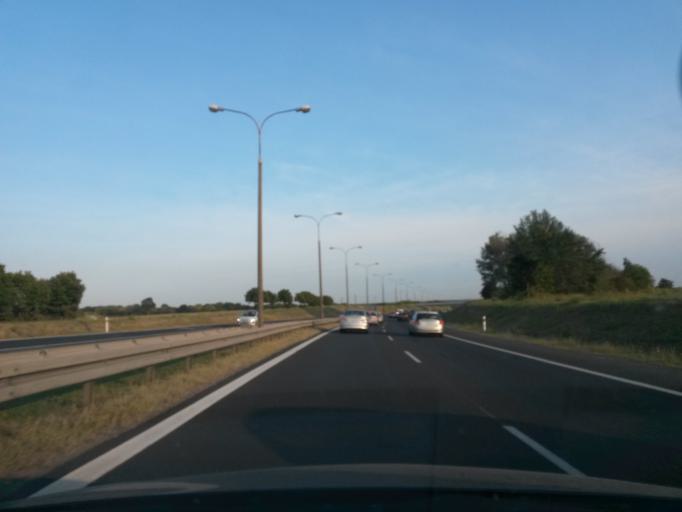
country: PL
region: Masovian Voivodeship
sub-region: Powiat nowodworski
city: Zakroczym
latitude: 52.4389
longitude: 20.6461
